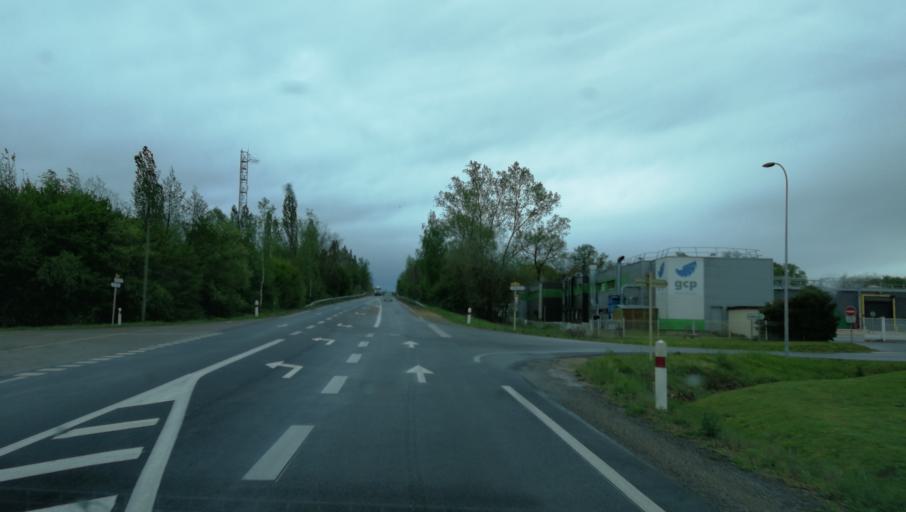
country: FR
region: Franche-Comte
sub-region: Departement du Jura
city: Bletterans
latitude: 46.7100
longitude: 5.4800
